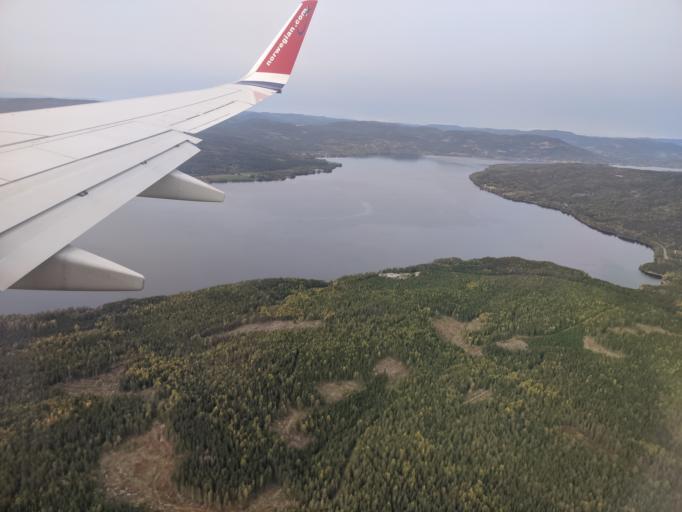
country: NO
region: Akershus
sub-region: Eidsvoll
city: Raholt
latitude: 60.3136
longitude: 11.1485
